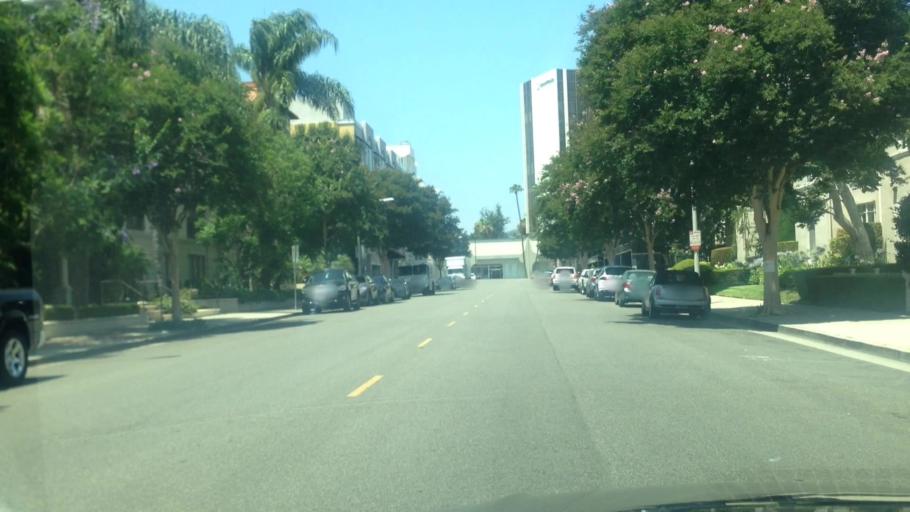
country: US
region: California
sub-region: Los Angeles County
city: Beverly Hills
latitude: 34.0653
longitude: -118.4089
